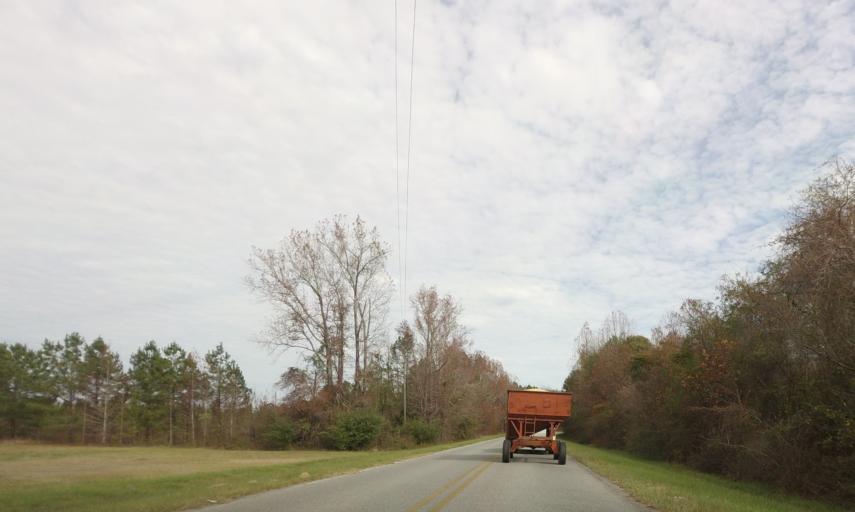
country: US
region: Georgia
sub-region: Dodge County
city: Chester
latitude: 32.4654
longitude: -83.1217
